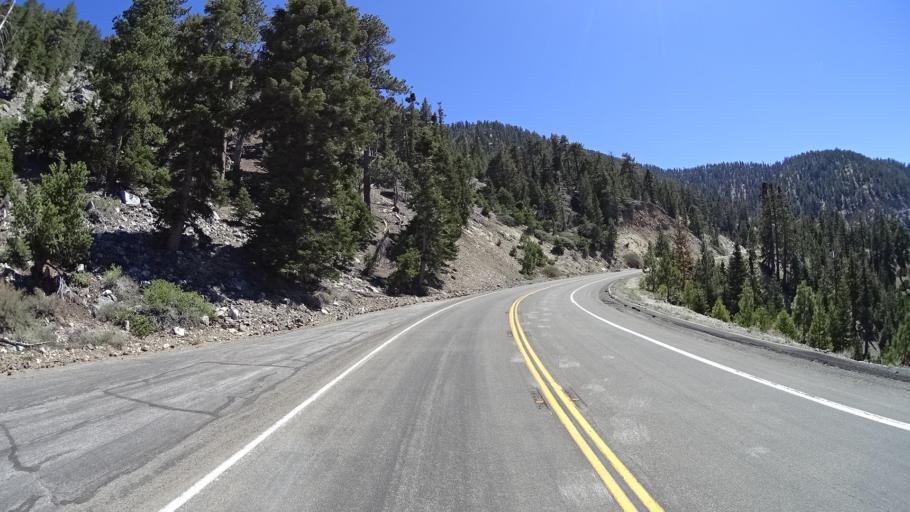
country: US
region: California
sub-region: San Bernardino County
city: Wrightwood
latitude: 34.3611
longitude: -117.7909
